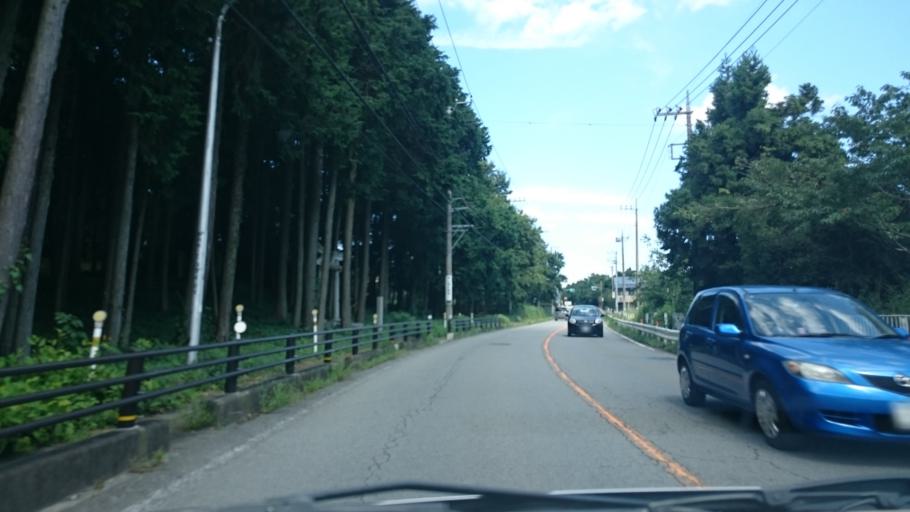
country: JP
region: Shizuoka
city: Gotemba
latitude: 35.2361
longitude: 138.9204
